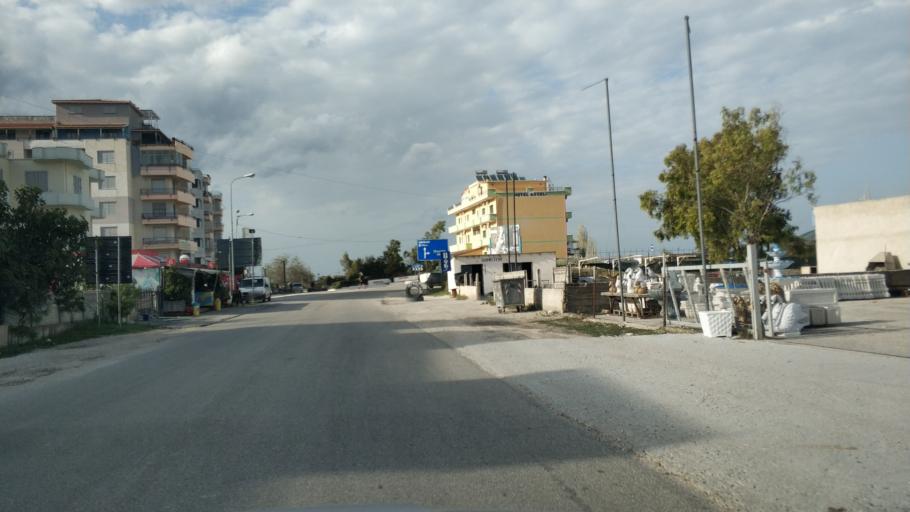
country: AL
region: Vlore
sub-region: Rrethi i Vlores
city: Orikum
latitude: 40.3307
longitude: 19.4768
